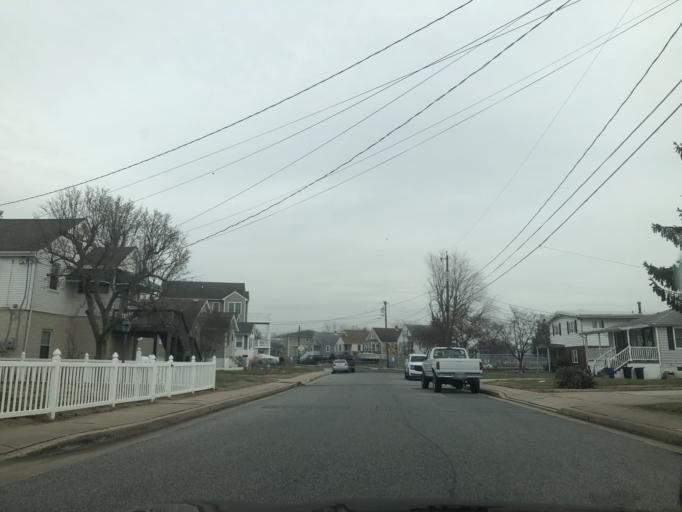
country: US
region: Maryland
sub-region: Baltimore County
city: Edgemere
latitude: 39.2593
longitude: -76.4813
